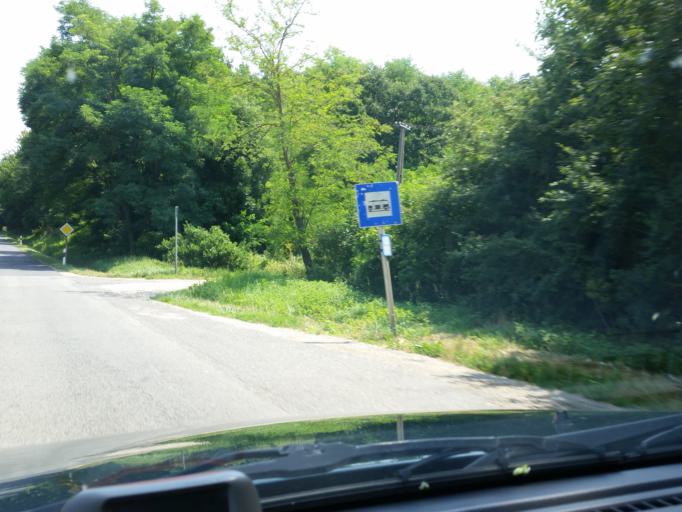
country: HU
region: Vas
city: Sarvar
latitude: 47.2364
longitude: 16.9965
